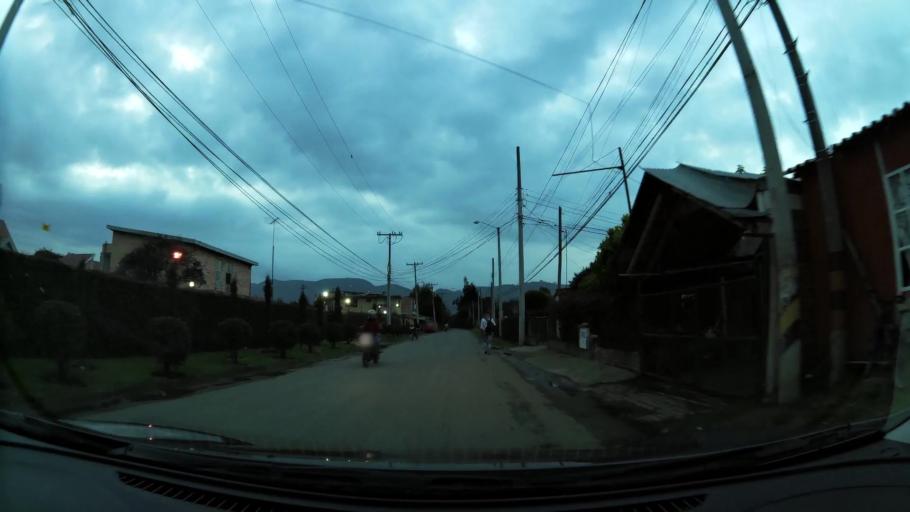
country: CO
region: Cundinamarca
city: Chia
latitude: 4.8398
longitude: -74.0604
